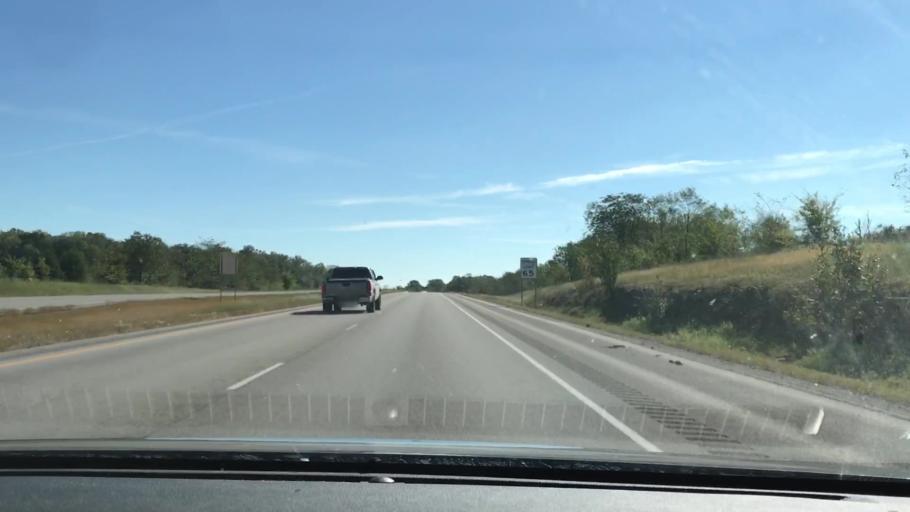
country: US
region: Kentucky
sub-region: Christian County
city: Hopkinsville
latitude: 36.8548
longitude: -87.4134
